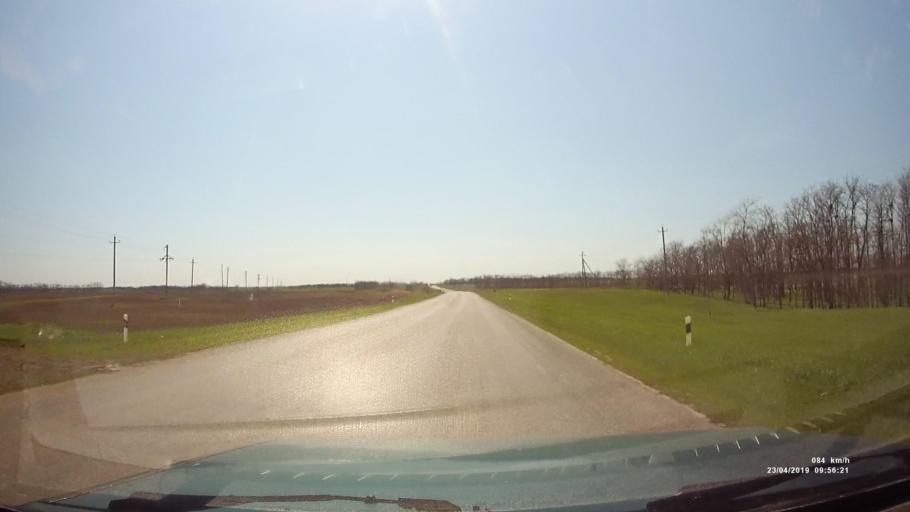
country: RU
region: Rostov
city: Orlovskiy
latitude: 46.7989
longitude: 42.0715
